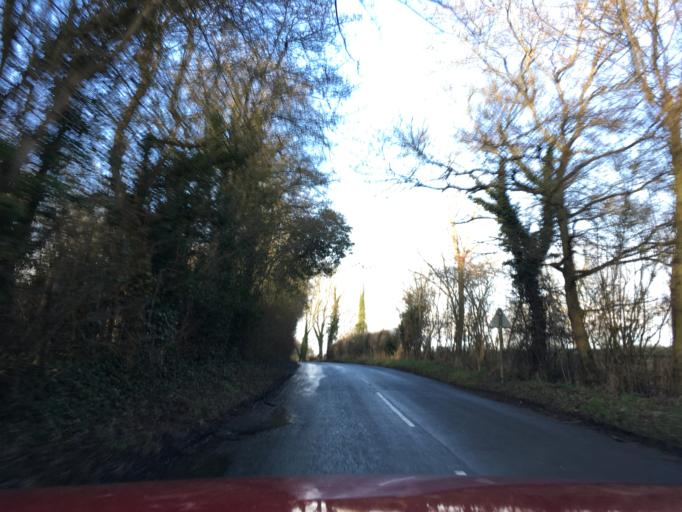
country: GB
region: England
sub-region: Warwickshire
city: Stratford-upon-Avon
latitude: 52.2231
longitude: -1.6891
